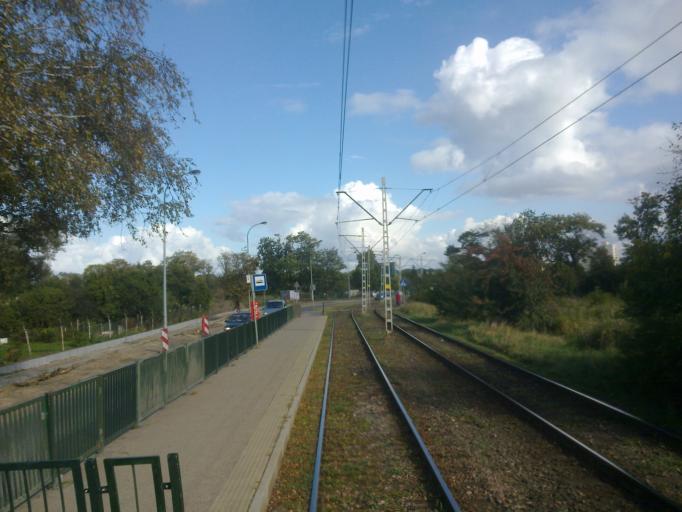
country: PL
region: Pomeranian Voivodeship
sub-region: Gdansk
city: Gdansk
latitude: 54.3626
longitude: 18.6982
